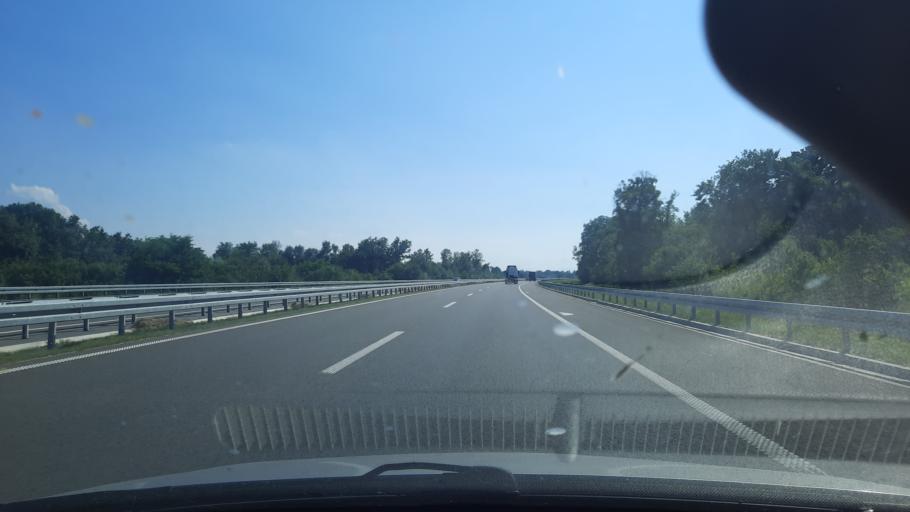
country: RS
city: Stubline
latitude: 44.5401
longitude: 20.1791
